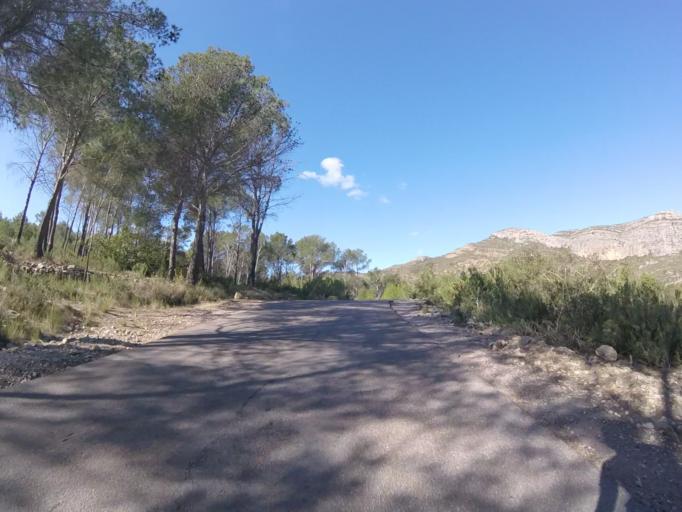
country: ES
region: Valencia
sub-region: Provincia de Castello
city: Orpesa/Oropesa del Mar
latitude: 40.0833
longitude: 0.1241
